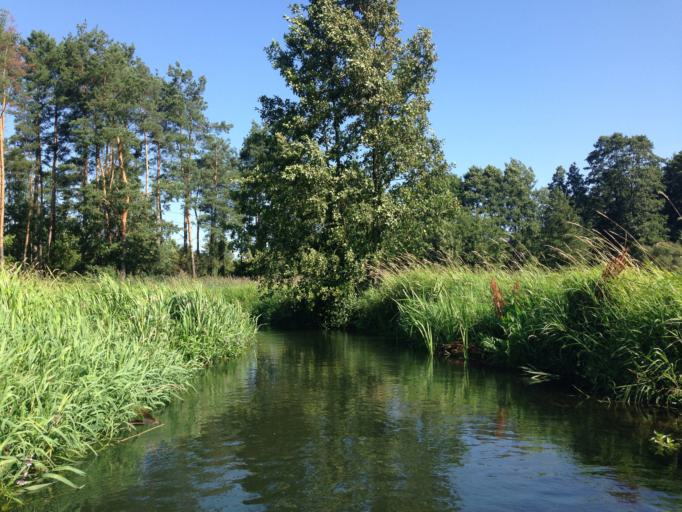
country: PL
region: Kujawsko-Pomorskie
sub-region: Powiat brodnicki
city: Bartniczka
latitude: 53.2547
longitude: 19.6038
